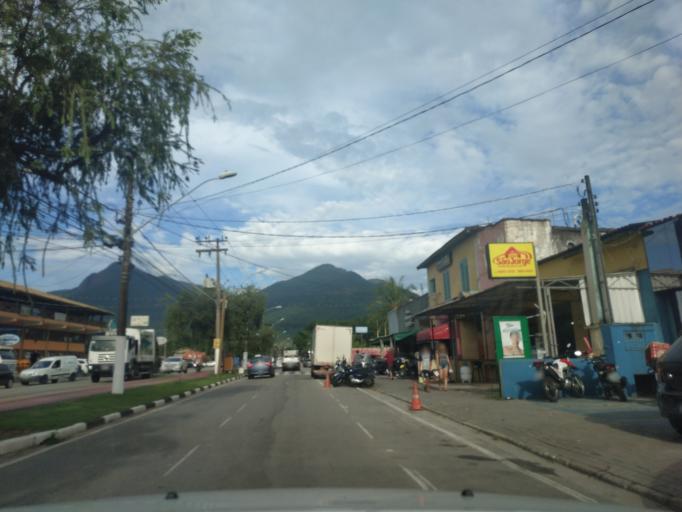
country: BR
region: Sao Paulo
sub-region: Ilhabela
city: Ilhabela
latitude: -23.8218
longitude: -45.3736
